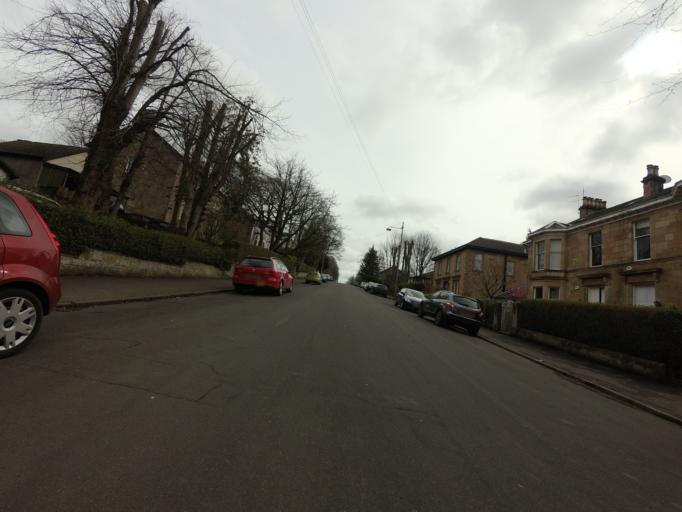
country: GB
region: Scotland
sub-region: Glasgow City
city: Glasgow
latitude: 55.8330
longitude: -4.2613
